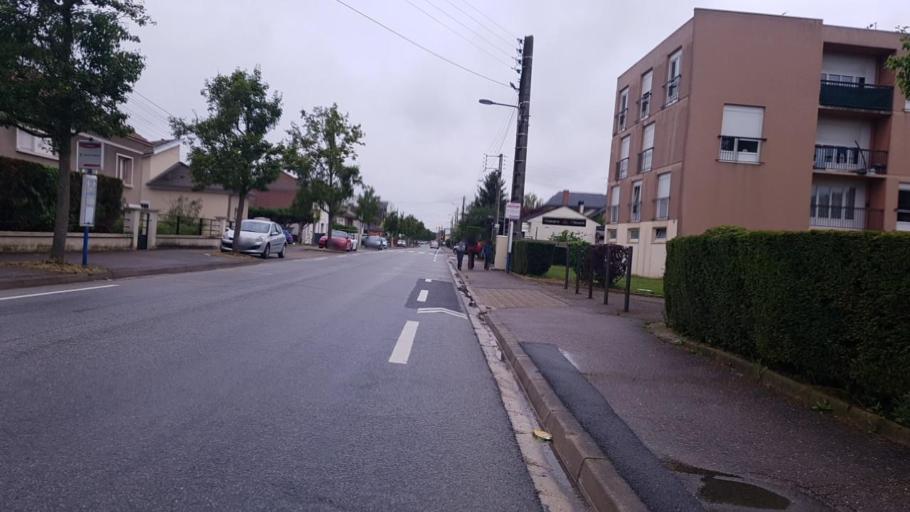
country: FR
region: Champagne-Ardenne
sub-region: Departement de la Marne
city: Saint-Memmie
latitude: 48.9369
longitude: 4.3851
